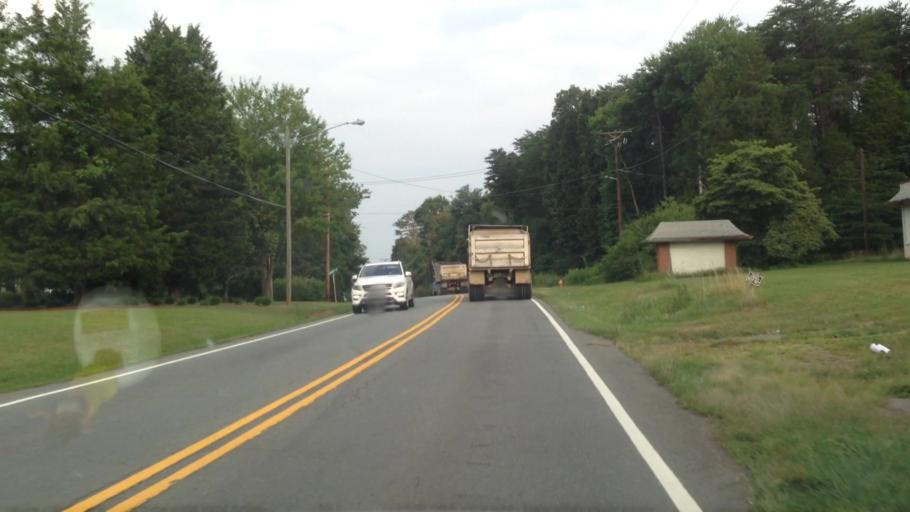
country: US
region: North Carolina
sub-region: Forsyth County
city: Rural Hall
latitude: 36.1944
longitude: -80.2513
